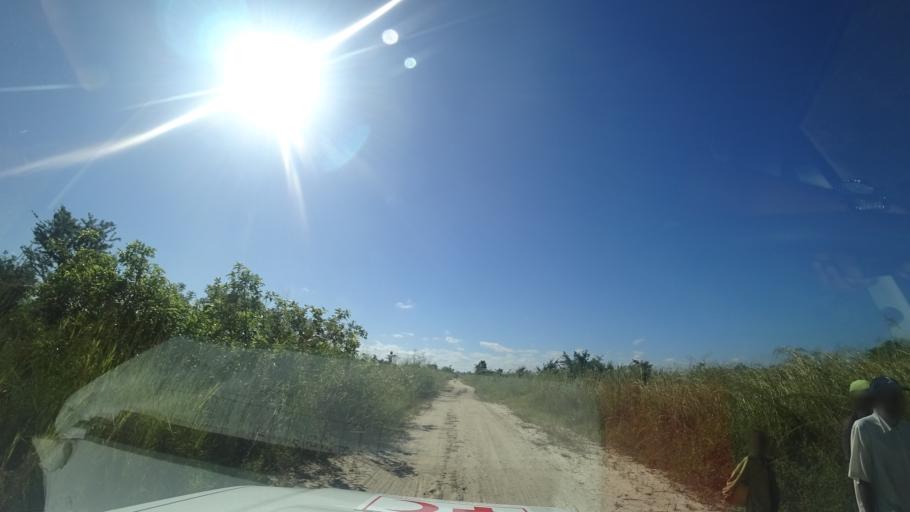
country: MZ
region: Sofala
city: Dondo
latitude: -19.3870
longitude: 34.5891
